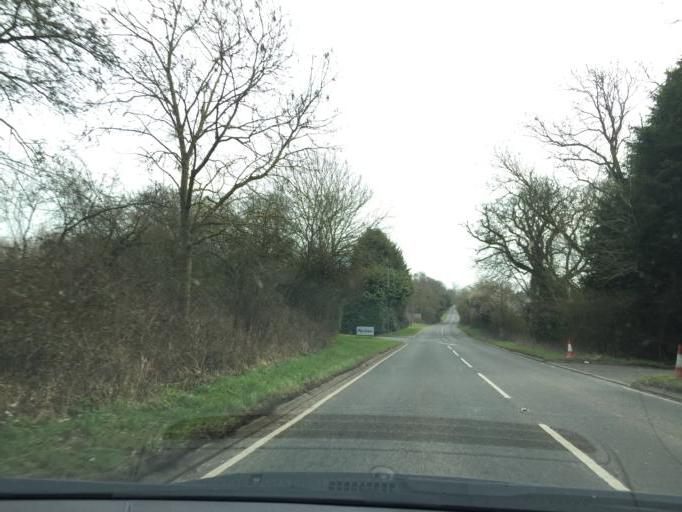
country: GB
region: England
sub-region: Warwickshire
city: Studley
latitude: 52.2986
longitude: -1.8601
